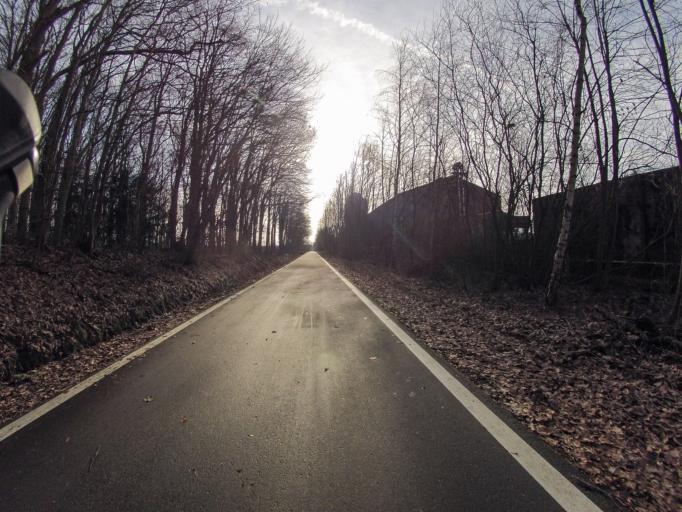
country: DE
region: North Rhine-Westphalia
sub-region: Regierungsbezirk Munster
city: Rheine
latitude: 52.2420
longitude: 7.4483
